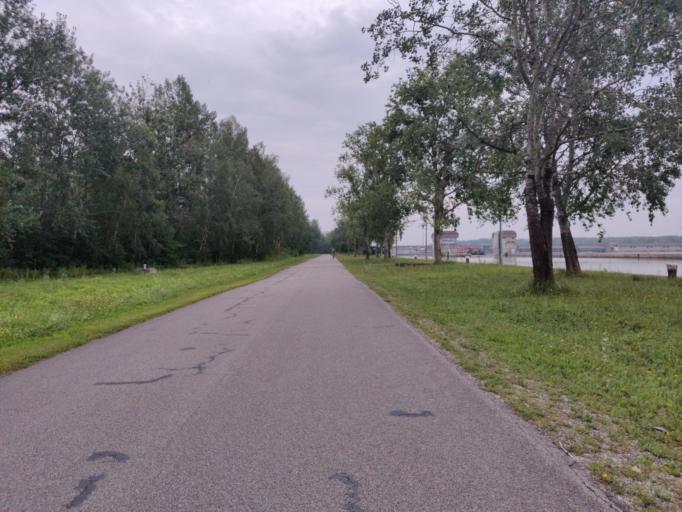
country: AT
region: Upper Austria
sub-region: Politischer Bezirk Linz-Land
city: Asten
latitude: 48.2531
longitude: 14.4269
